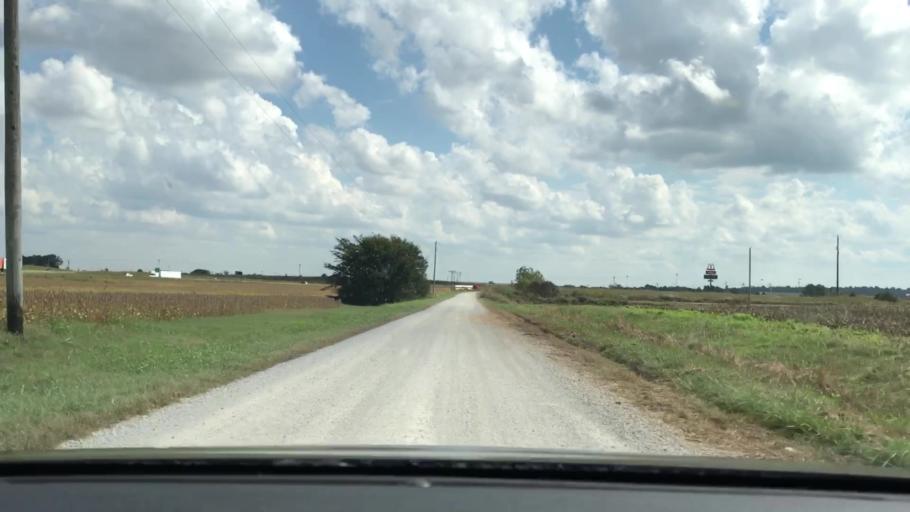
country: US
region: Kentucky
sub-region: Christian County
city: Oak Grove
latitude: 36.6831
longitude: -87.4113
